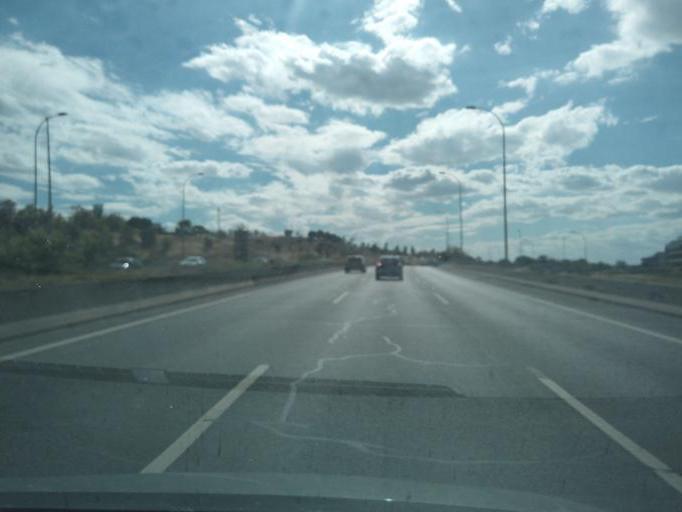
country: ES
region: Madrid
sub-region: Provincia de Madrid
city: San Sebastian de los Reyes
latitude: 40.5332
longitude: -3.6174
